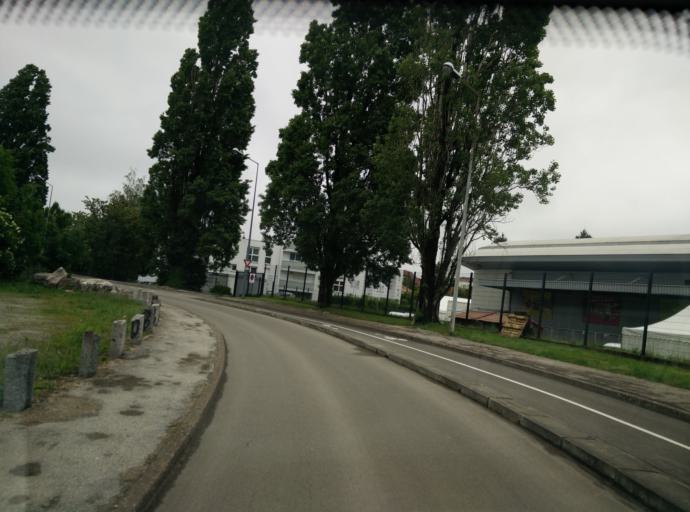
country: FR
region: Franche-Comte
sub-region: Departement du Doubs
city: Beure
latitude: 47.2266
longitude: 5.9825
